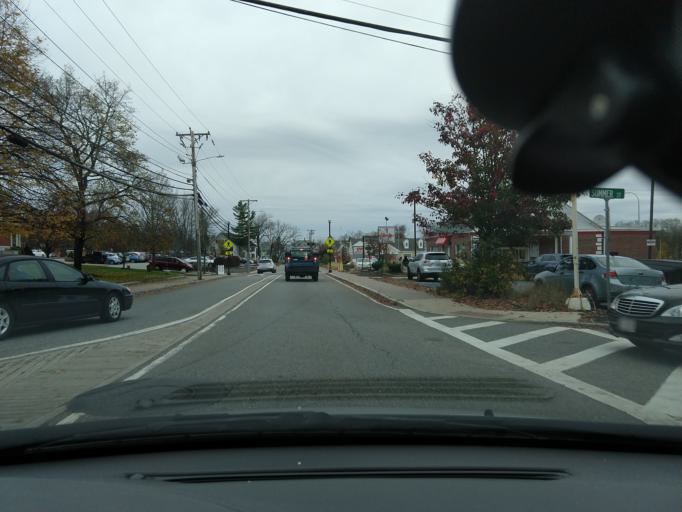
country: US
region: Massachusetts
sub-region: Middlesex County
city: Chelmsford
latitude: 42.5935
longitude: -71.3512
